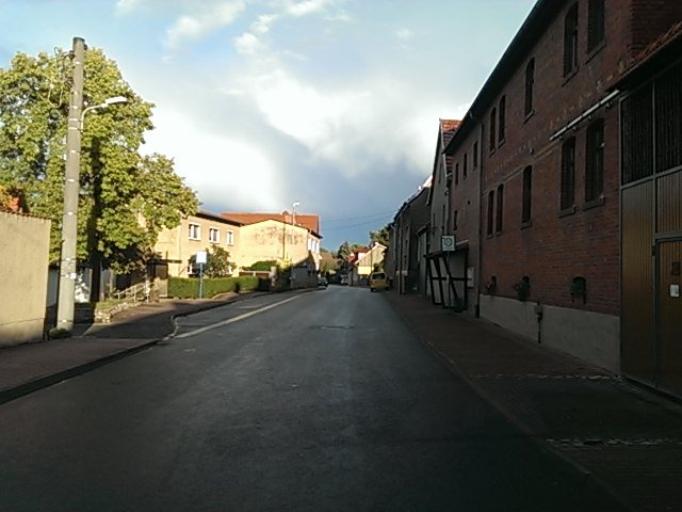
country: DE
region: Thuringia
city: Ostramondra
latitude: 51.1985
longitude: 11.3233
